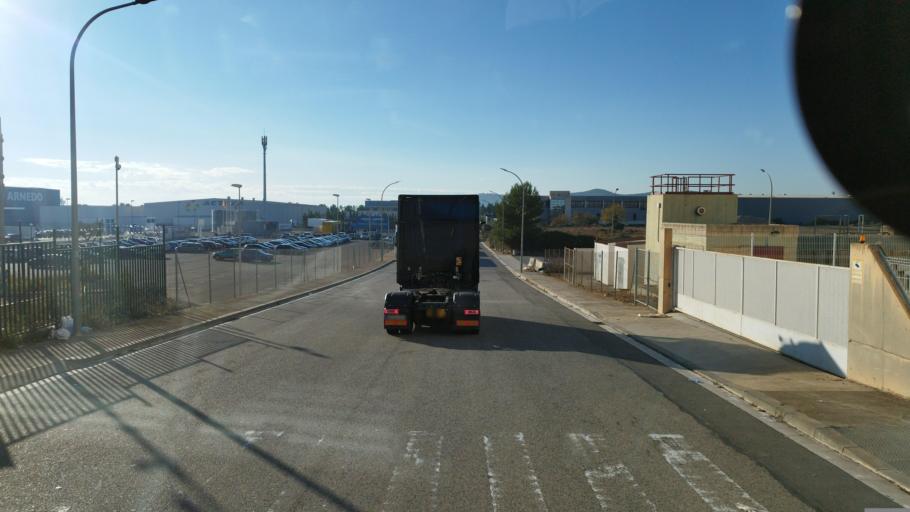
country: ES
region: Catalonia
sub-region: Provincia de Tarragona
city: la Bisbal del Penedes
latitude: 41.2725
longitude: 1.5167
